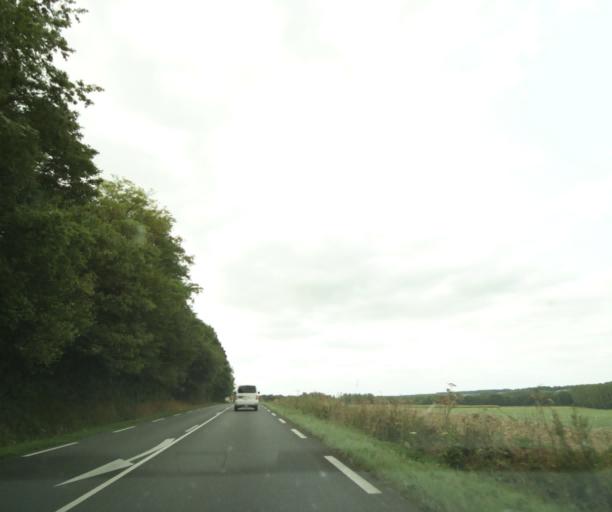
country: FR
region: Centre
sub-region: Departement d'Indre-et-Loire
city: Chambourg-sur-Indre
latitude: 47.1673
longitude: 0.9822
